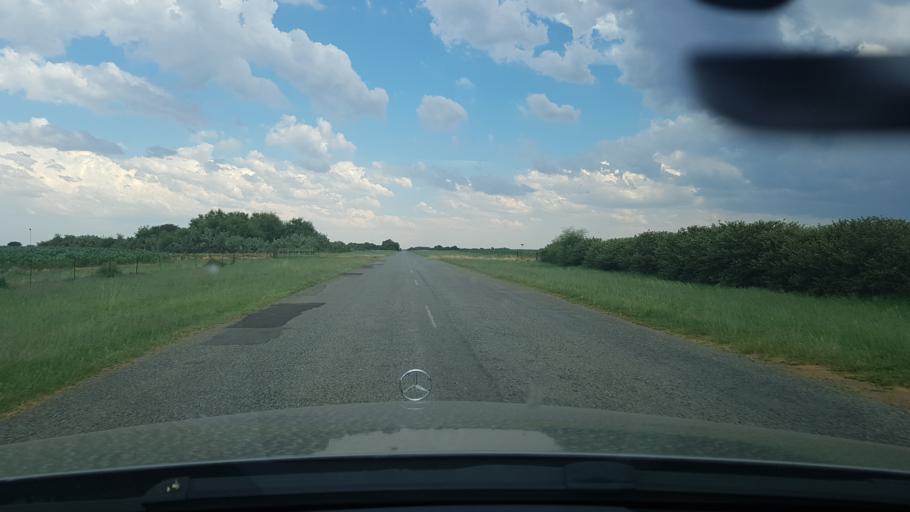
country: ZA
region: Orange Free State
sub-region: Lejweleputswa District Municipality
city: Hoopstad
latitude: -27.9200
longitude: 25.6855
